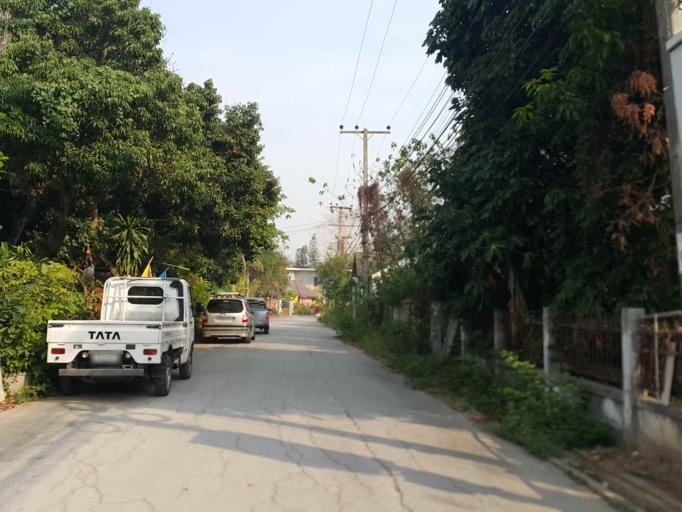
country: TH
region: Chiang Mai
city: Saraphi
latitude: 18.7698
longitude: 99.0620
